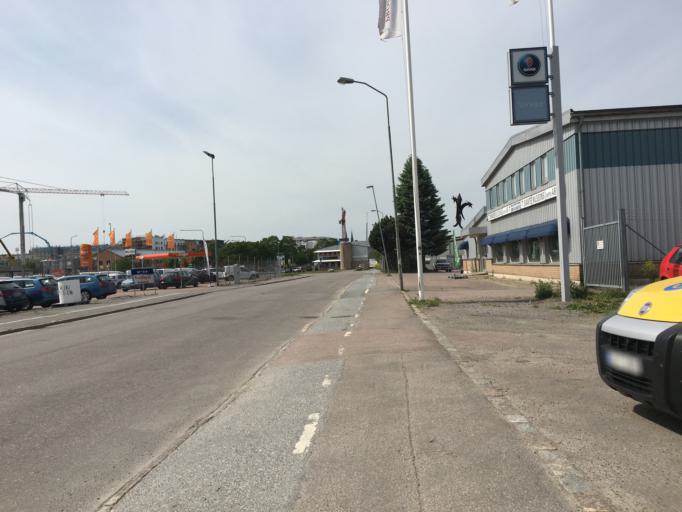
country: SE
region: Uppsala
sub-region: Uppsala Kommun
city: Uppsala
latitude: 59.8491
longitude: 17.6631
